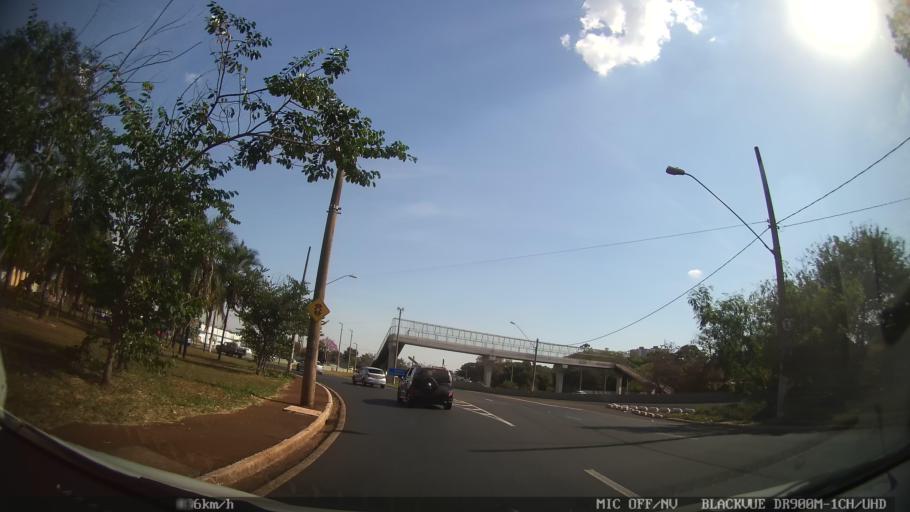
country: BR
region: Sao Paulo
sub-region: Ribeirao Preto
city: Ribeirao Preto
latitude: -21.1776
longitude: -47.8231
